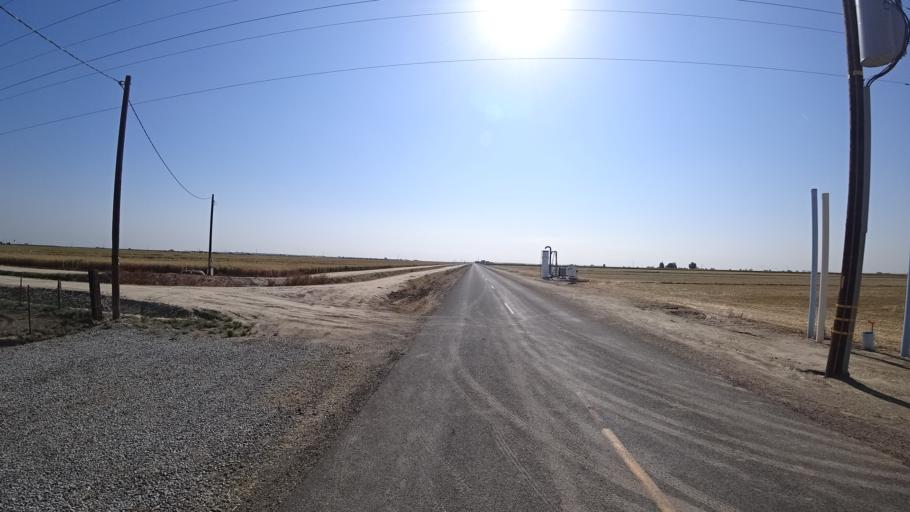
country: US
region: California
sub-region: Kings County
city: Home Garden
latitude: 36.2404
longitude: -119.5921
